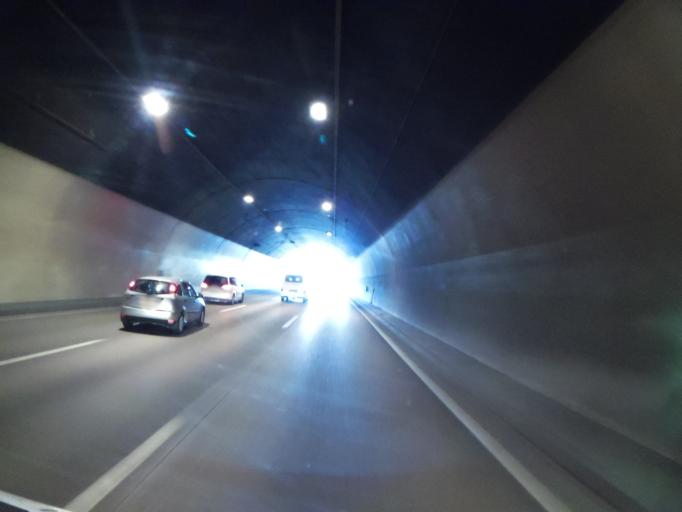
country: AT
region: Styria
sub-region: Politischer Bezirk Graz-Umgebung
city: Gratkorn
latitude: 47.1268
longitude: 15.3645
